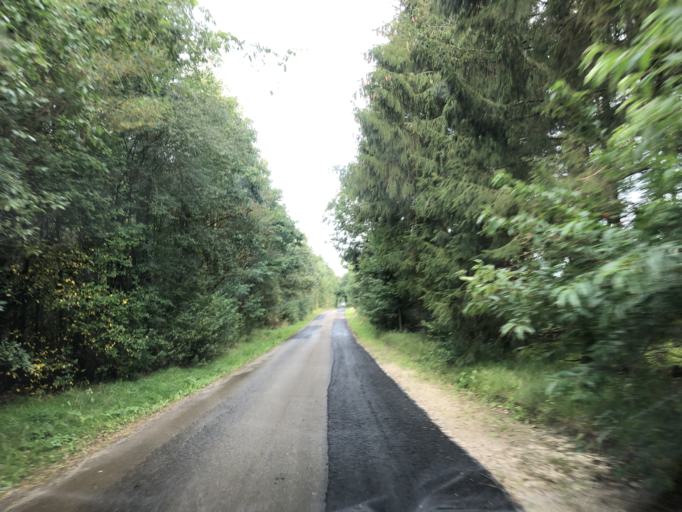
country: DK
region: Central Jutland
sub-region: Holstebro Kommune
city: Ulfborg
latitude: 56.3030
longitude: 8.4372
